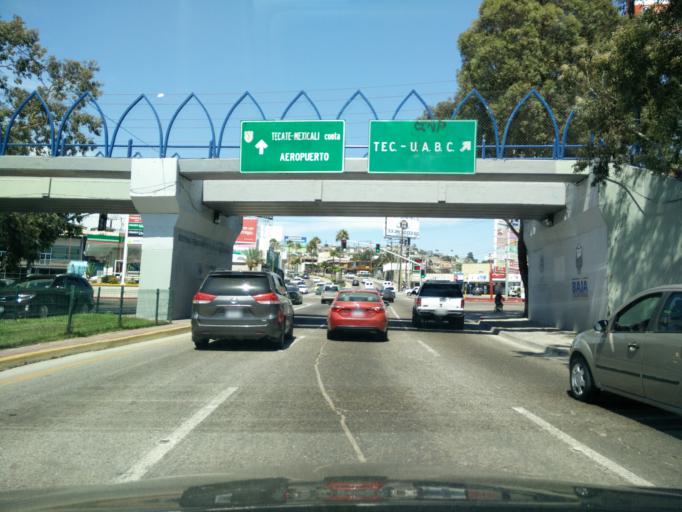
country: MX
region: Baja California
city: Tijuana
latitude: 32.5305
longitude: -117.0125
